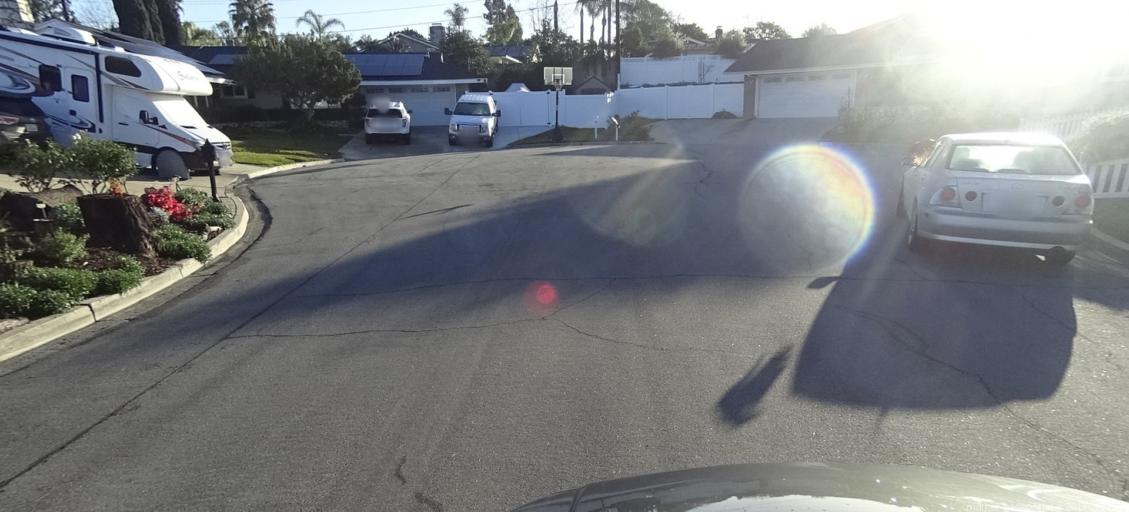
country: US
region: California
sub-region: Orange County
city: North Tustin
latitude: 33.7686
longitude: -117.8102
